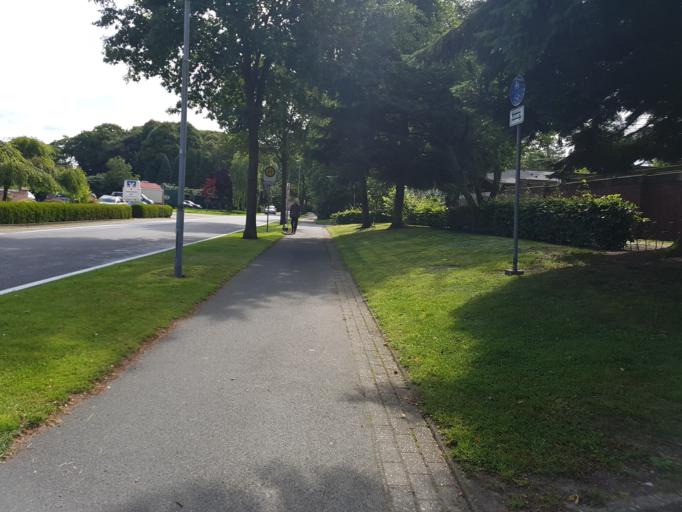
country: DE
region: Lower Saxony
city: Wittmund
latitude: 53.5304
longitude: 7.7777
